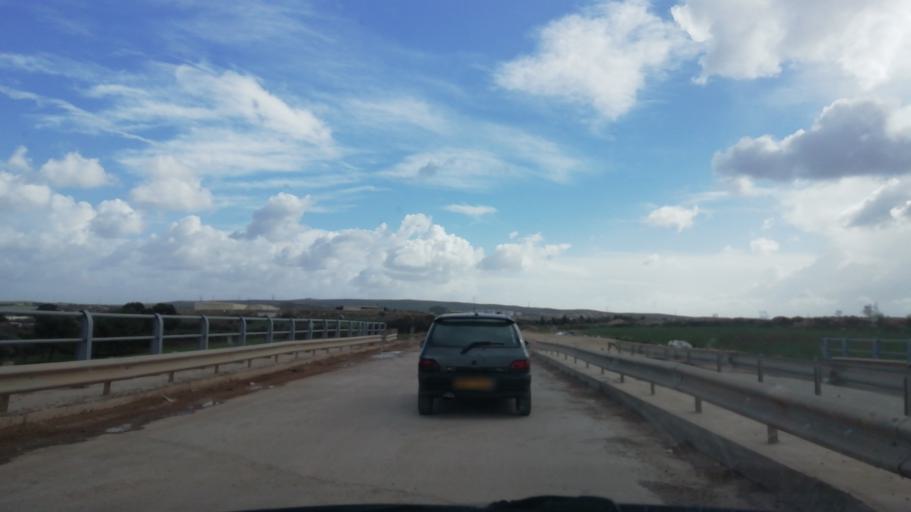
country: DZ
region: Oran
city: Sidi ech Chahmi
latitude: 35.6352
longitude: -0.5380
